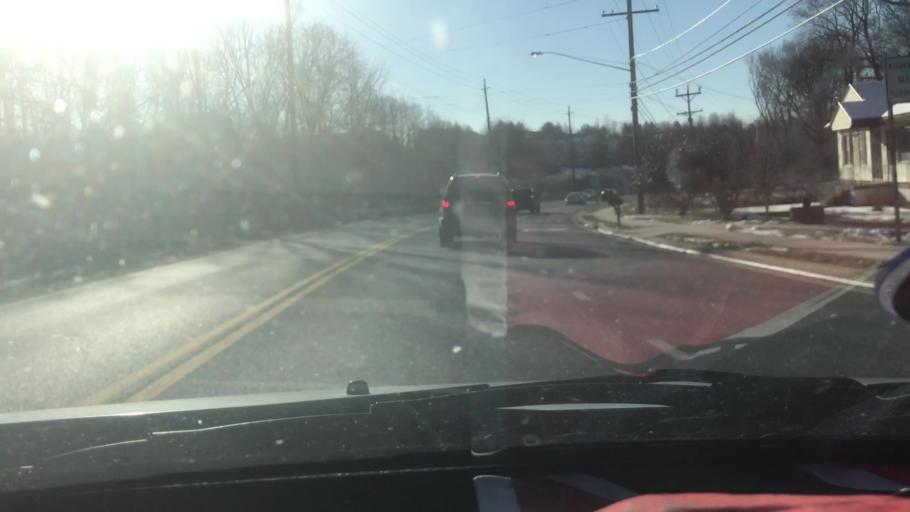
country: US
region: Maryland
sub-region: Prince George's County
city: Suitland
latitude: 38.8444
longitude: -76.9169
